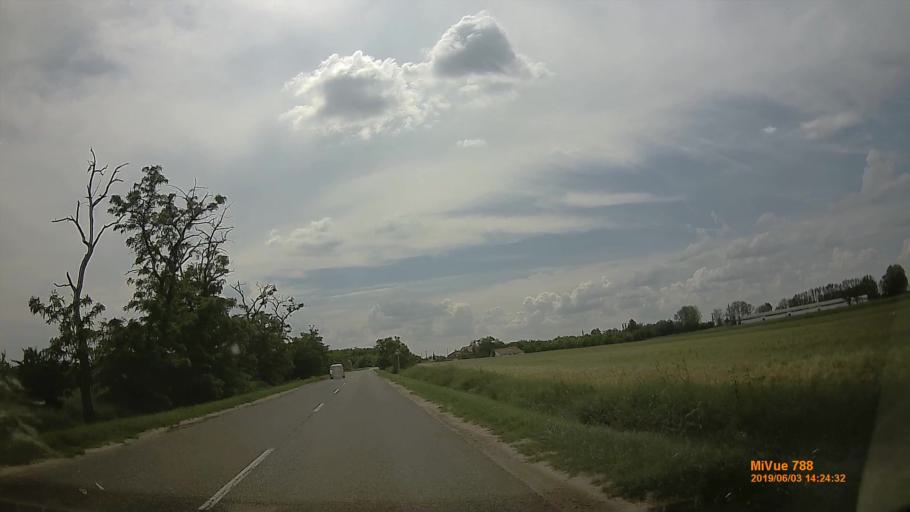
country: HU
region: Pest
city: Jaszkarajeno
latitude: 47.0145
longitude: 20.1300
